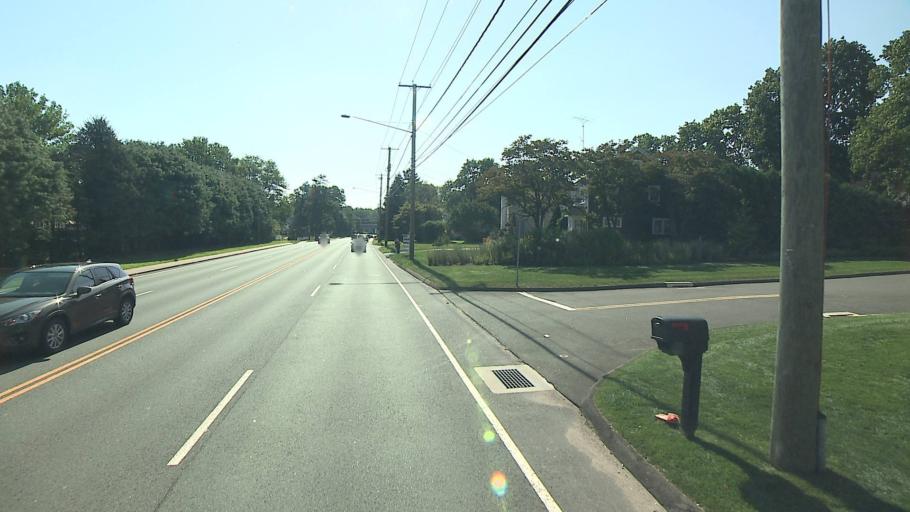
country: US
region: Connecticut
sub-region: Fairfield County
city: Trumbull
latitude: 41.2434
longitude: -73.1940
